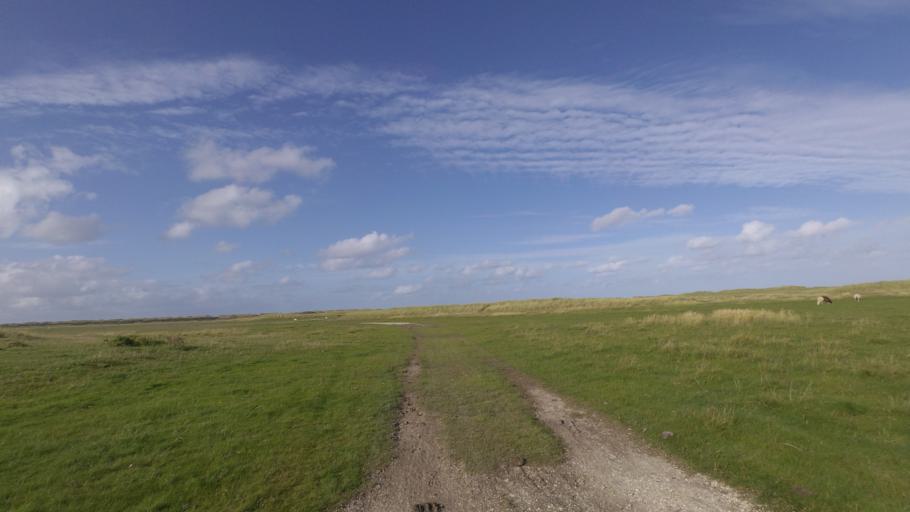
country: NL
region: Friesland
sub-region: Gemeente Ameland
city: Nes
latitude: 53.4528
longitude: 5.8622
